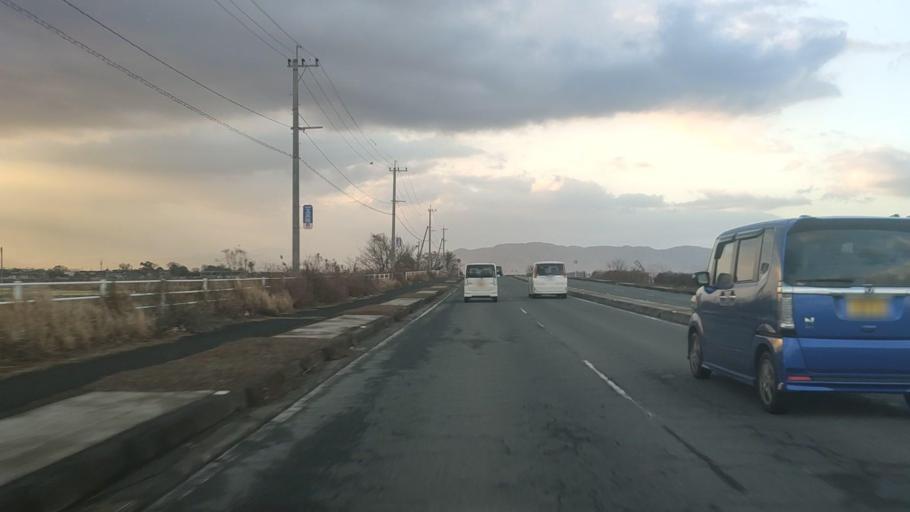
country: JP
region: Kumamoto
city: Kumamoto
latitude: 32.7546
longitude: 130.7064
